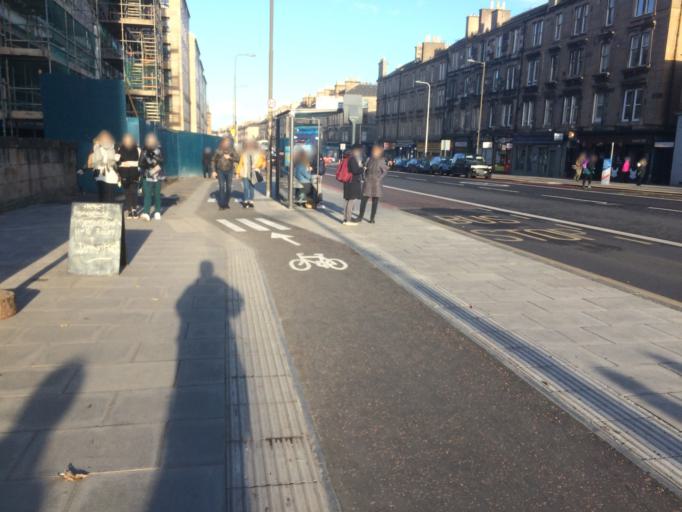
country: GB
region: Scotland
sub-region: Edinburgh
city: Edinburgh
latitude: 55.9620
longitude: -3.1802
